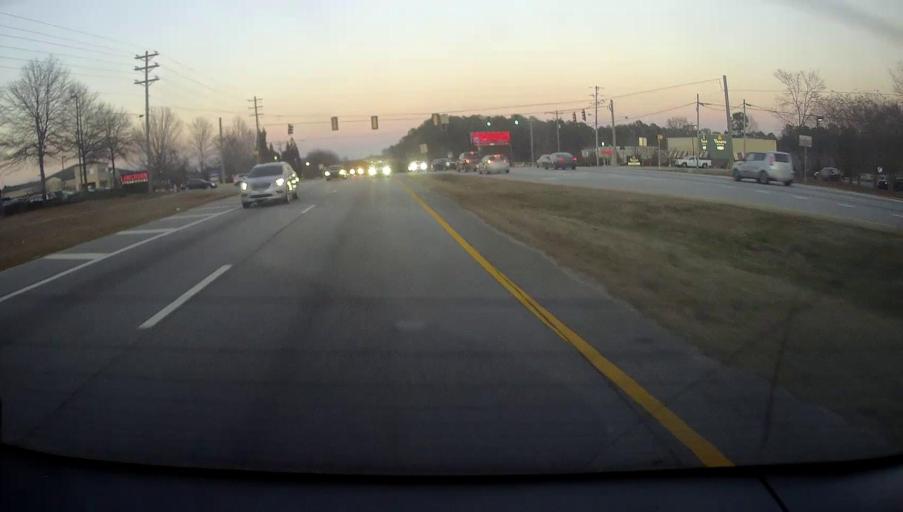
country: US
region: Georgia
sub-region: Fayette County
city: Fayetteville
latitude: 33.4753
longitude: -84.4404
